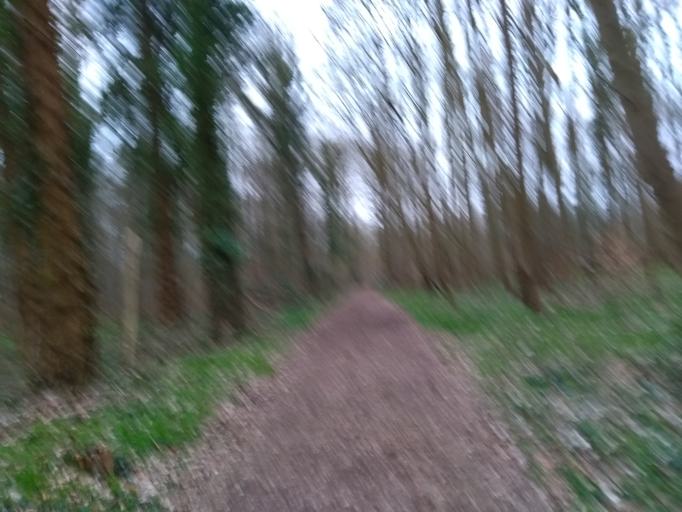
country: FR
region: Picardie
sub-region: Departement de l'Oise
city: Choisy-au-Bac
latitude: 49.4381
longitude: 2.8894
